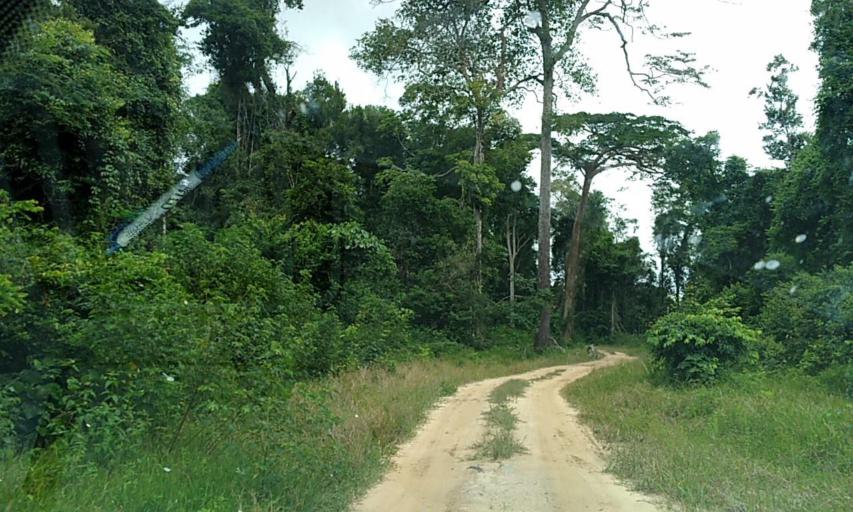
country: BR
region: Para
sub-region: Altamira
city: Altamira
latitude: -3.0459
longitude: -52.9024
